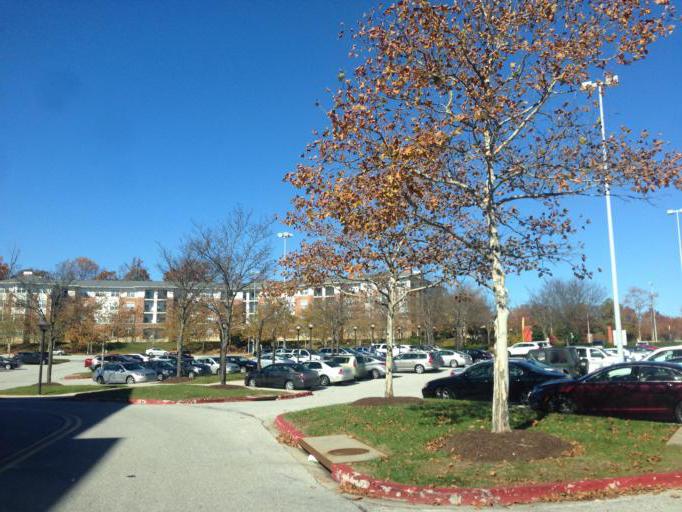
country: US
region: Maryland
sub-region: Howard County
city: Columbia
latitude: 39.2177
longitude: -76.8612
